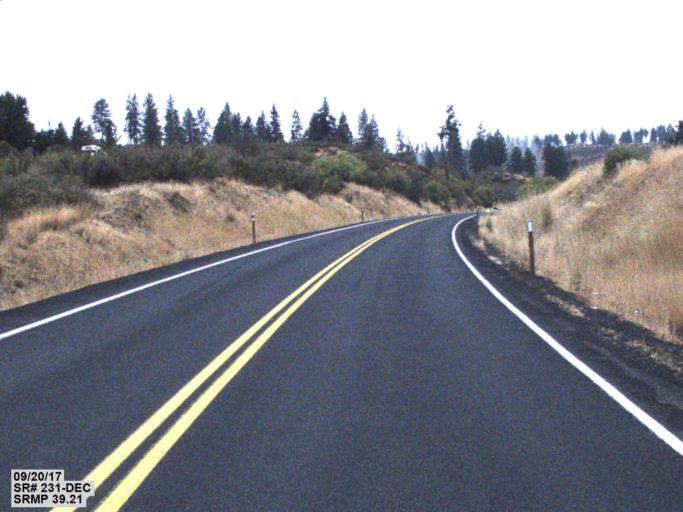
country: US
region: Washington
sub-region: Lincoln County
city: Davenport
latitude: 47.7779
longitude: -117.8892
